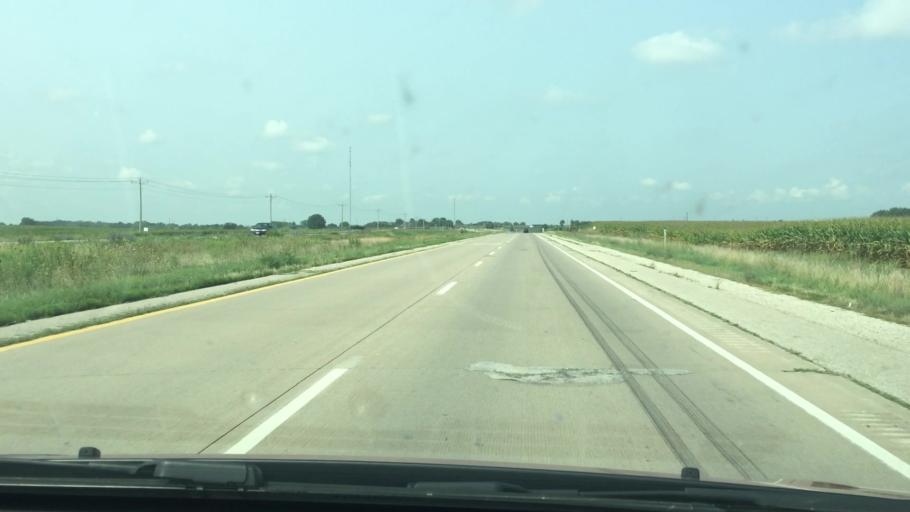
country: US
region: Iowa
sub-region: Cedar County
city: Durant
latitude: 41.5197
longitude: -90.8660
